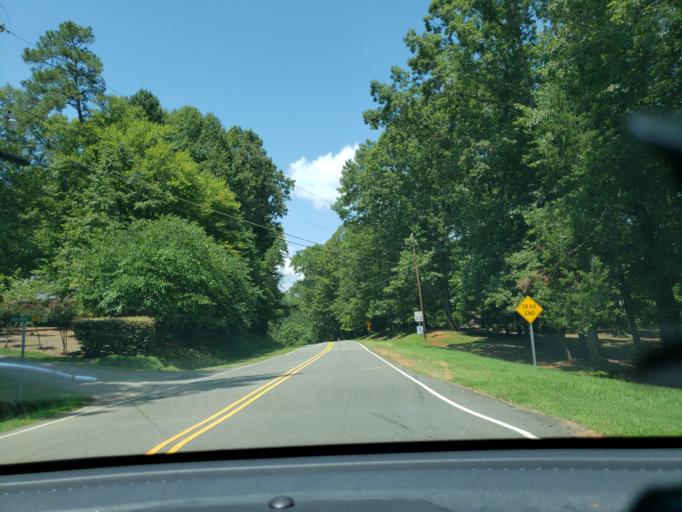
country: US
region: North Carolina
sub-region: Orange County
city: Hillsborough
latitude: 36.0683
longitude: -78.9968
